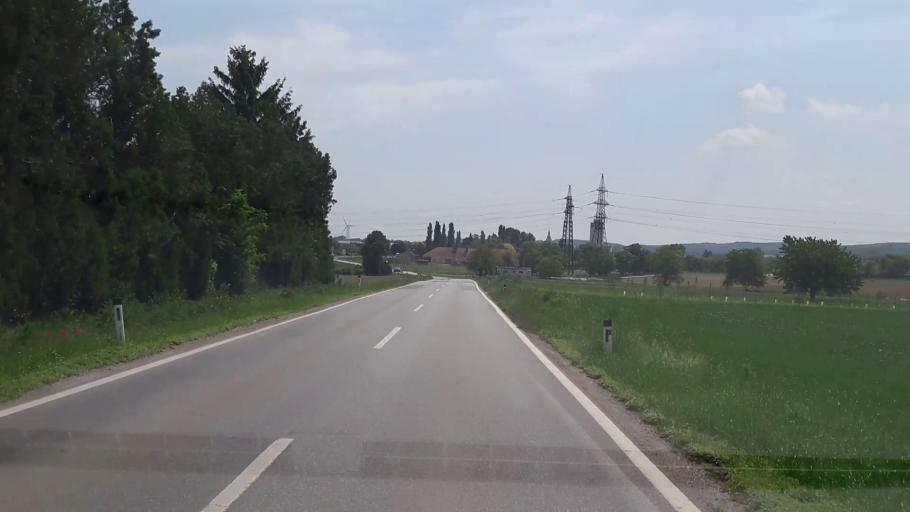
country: AT
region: Lower Austria
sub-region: Politischer Bezirk Bruck an der Leitha
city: Bruck an der Leitha
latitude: 48.0357
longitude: 16.7617
